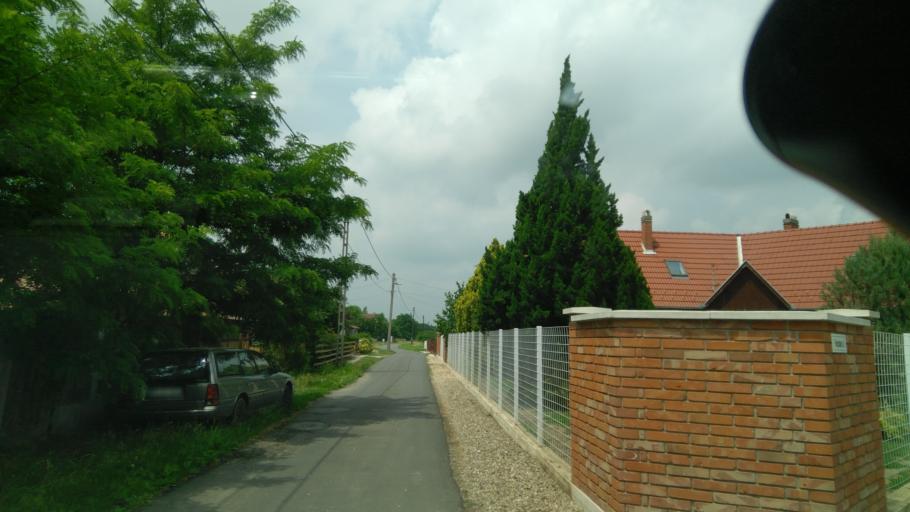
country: HU
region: Bekes
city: Gyula
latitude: 46.6599
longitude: 21.2568
